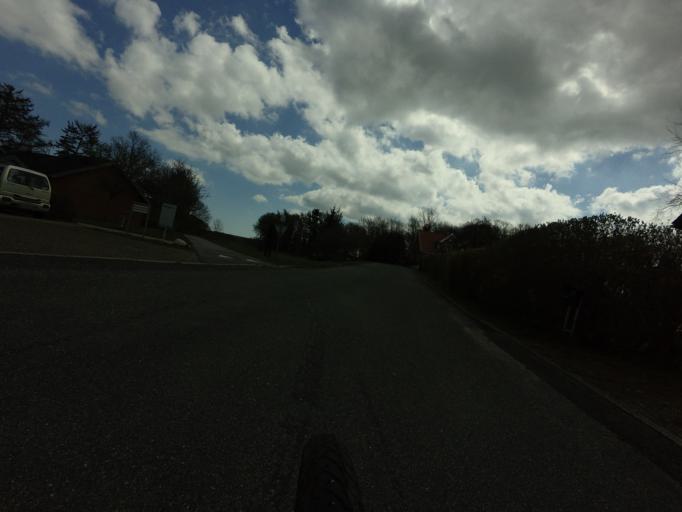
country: DK
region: North Denmark
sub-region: Mariagerfjord Kommune
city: Hadsund
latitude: 56.8271
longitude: 10.1250
